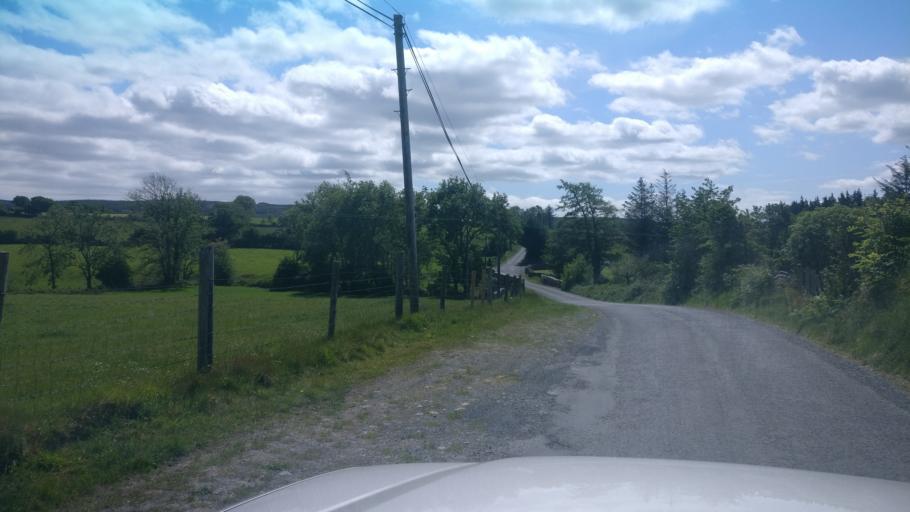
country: IE
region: Connaught
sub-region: County Galway
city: Gort
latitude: 53.1409
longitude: -8.7232
